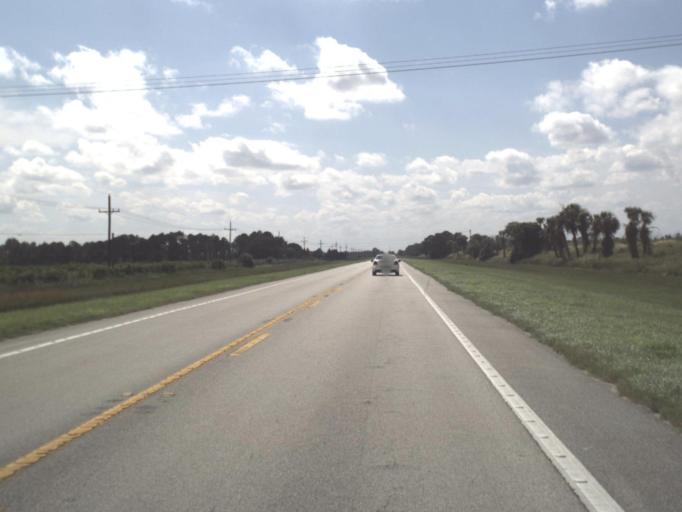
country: US
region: Florida
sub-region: Hendry County
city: Port LaBelle
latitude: 26.6318
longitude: -81.4364
